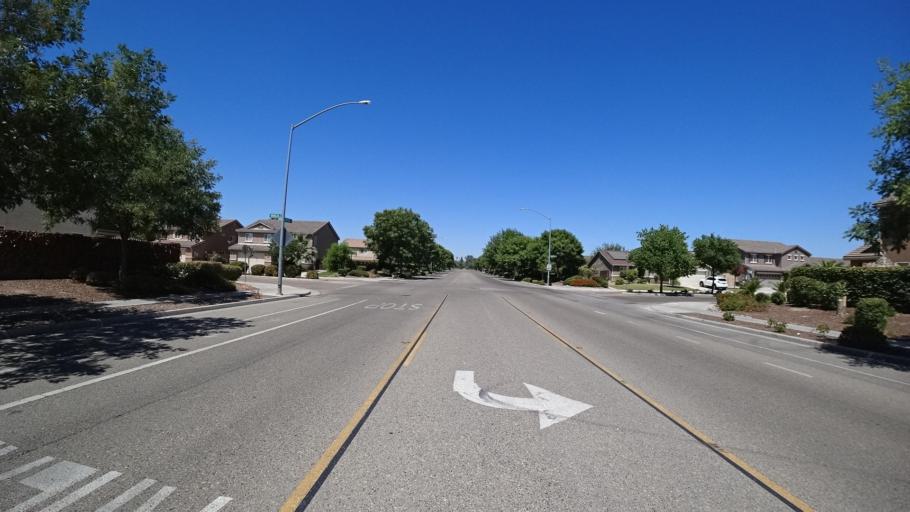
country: US
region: California
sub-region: Fresno County
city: Sunnyside
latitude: 36.7259
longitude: -119.6744
